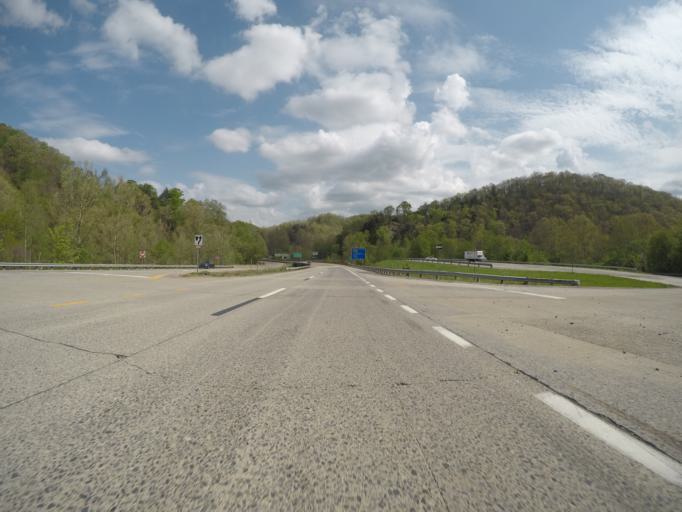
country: US
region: West Virginia
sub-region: Kanawha County
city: Alum Creek
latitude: 38.1798
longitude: -81.8492
